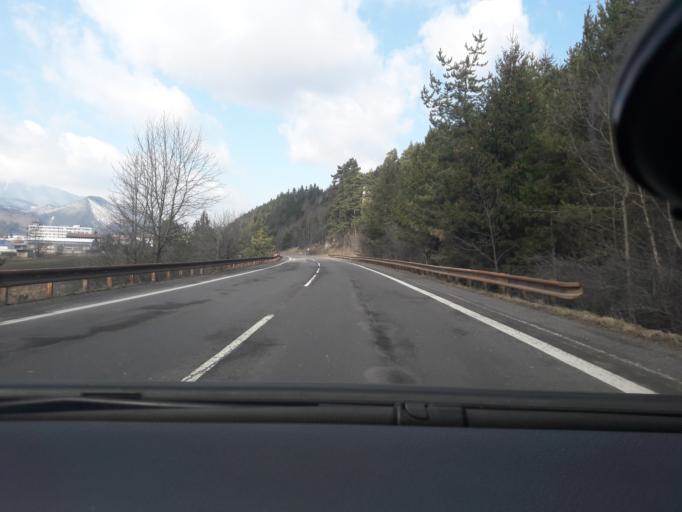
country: SK
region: Zilinsky
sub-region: Okres Zilina
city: Liptovsky Hradok
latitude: 49.0372
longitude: 19.7542
